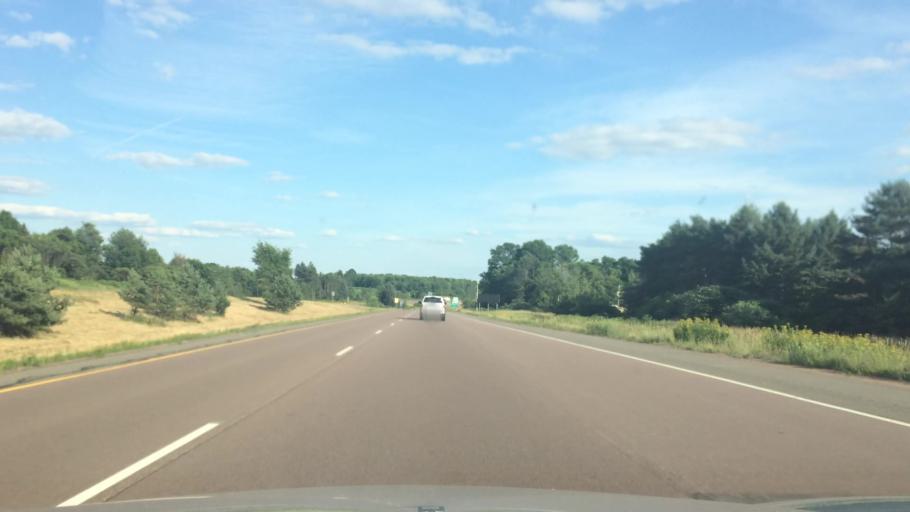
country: US
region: Wisconsin
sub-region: Marathon County
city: Wausau
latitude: 45.0131
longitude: -89.6661
